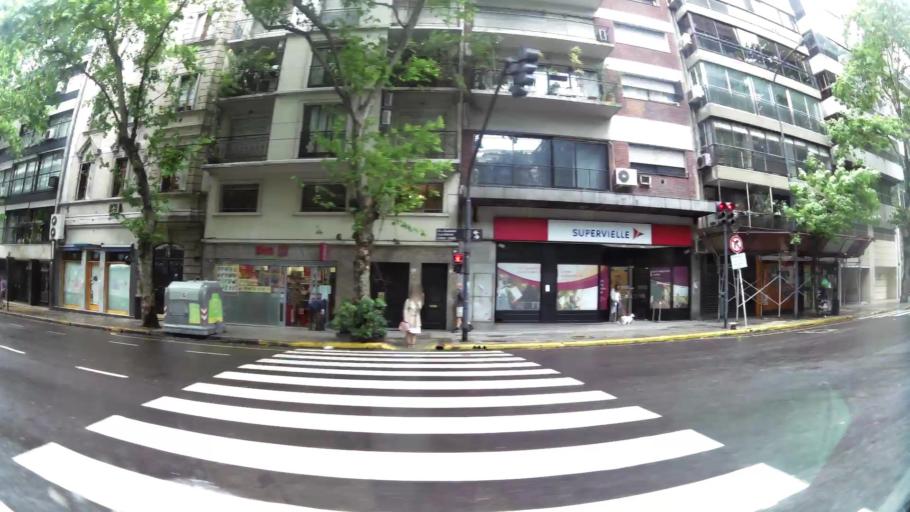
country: AR
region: Buenos Aires F.D.
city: Retiro
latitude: -34.5865
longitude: -58.3982
